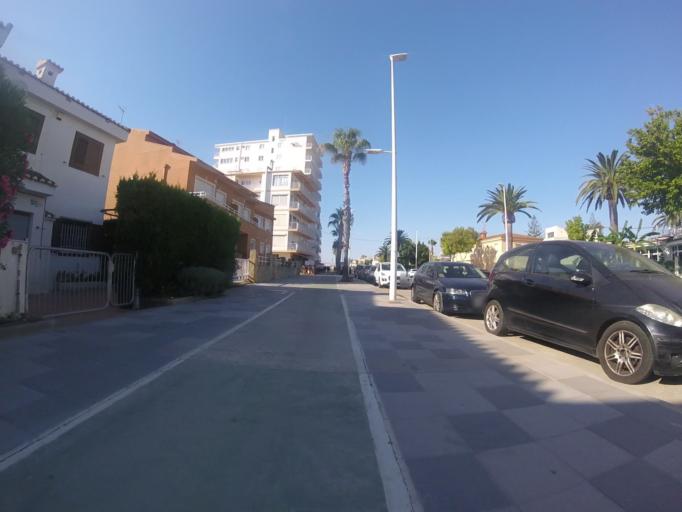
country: ES
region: Valencia
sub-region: Provincia de Castello
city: Benicarlo
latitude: 40.4018
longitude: 0.4181
